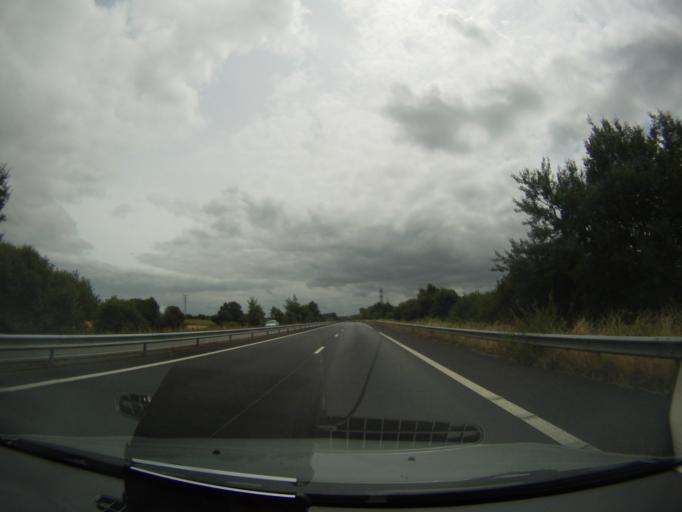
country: FR
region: Pays de la Loire
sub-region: Departement de la Loire-Atlantique
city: Derval
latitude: 47.6546
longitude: -1.6712
